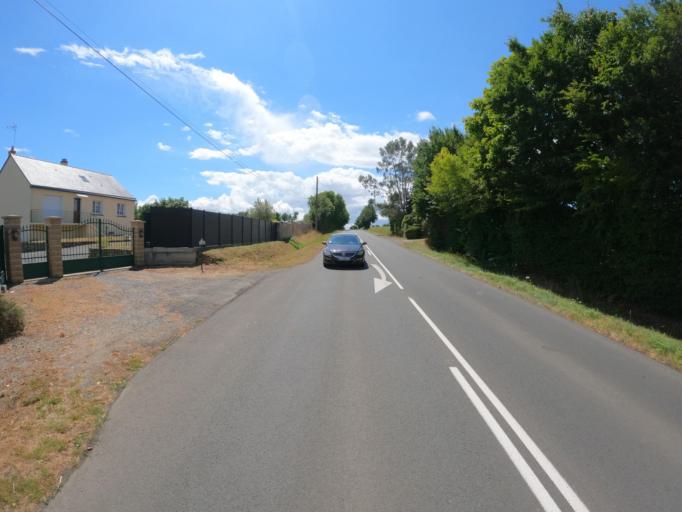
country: FR
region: Pays de la Loire
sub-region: Departement de Maine-et-Loire
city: Champigne
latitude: 47.6527
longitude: -0.5756
